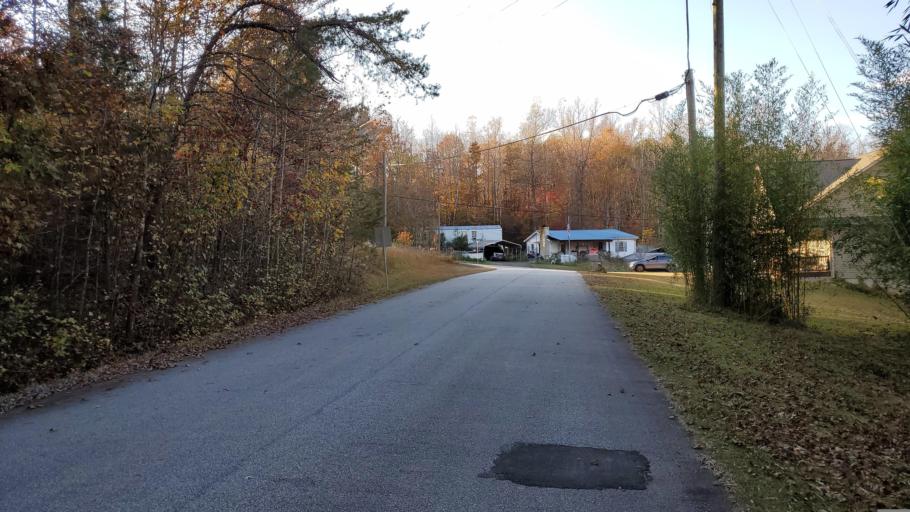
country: US
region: South Carolina
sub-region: Greenville County
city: Tigerville
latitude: 35.0713
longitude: -82.3294
